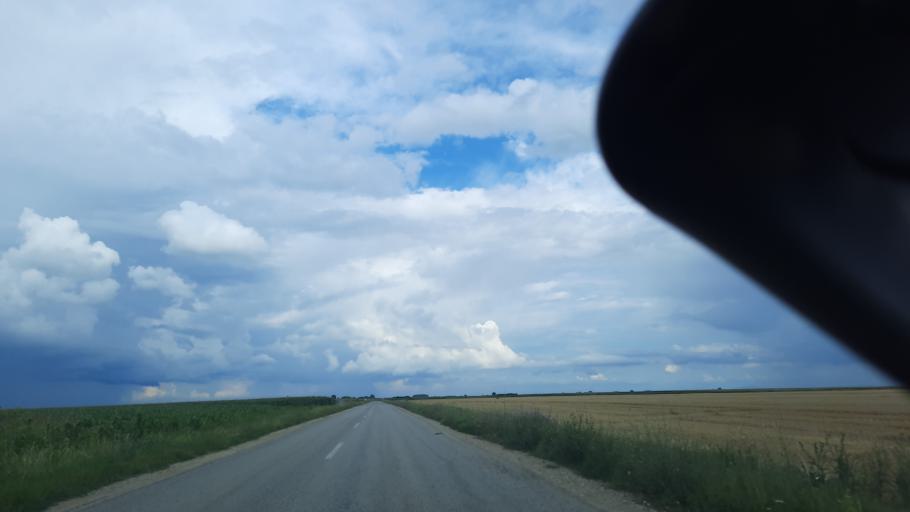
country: RS
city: Putinci
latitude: 44.9901
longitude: 19.9990
